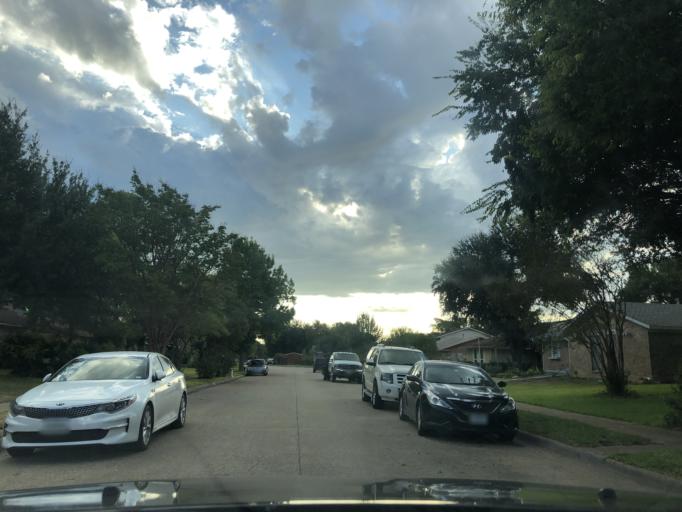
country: US
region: Texas
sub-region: Dallas County
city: Garland
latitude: 32.8744
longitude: -96.6555
